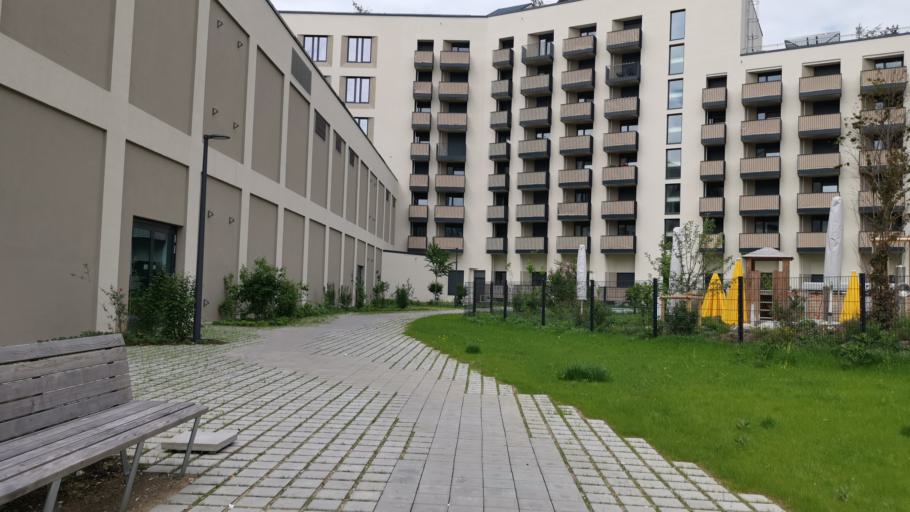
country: DE
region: Bavaria
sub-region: Upper Bavaria
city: Pullach im Isartal
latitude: 48.0950
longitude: 11.5093
